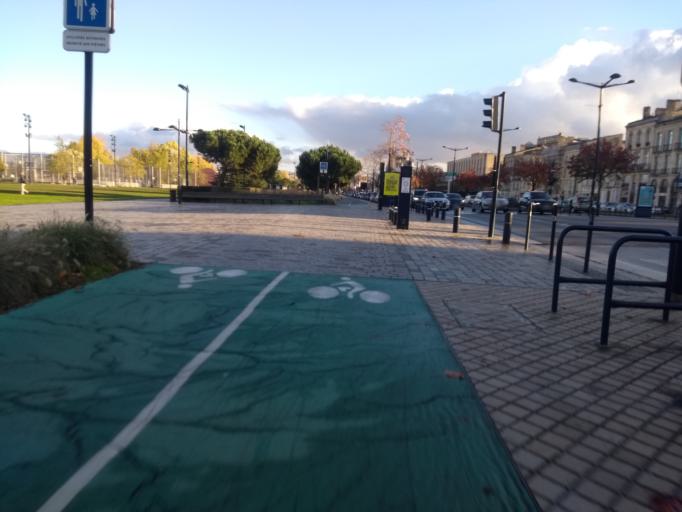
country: FR
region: Aquitaine
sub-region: Departement de la Gironde
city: Bordeaux
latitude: 44.8336
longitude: -0.5617
